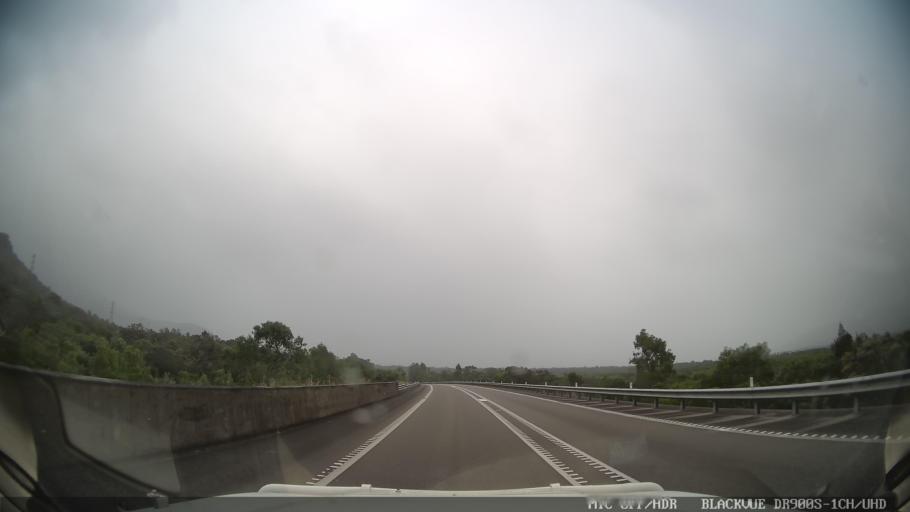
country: AU
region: Queensland
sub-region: Hinchinbrook
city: Ingham
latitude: -18.5097
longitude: 146.1880
